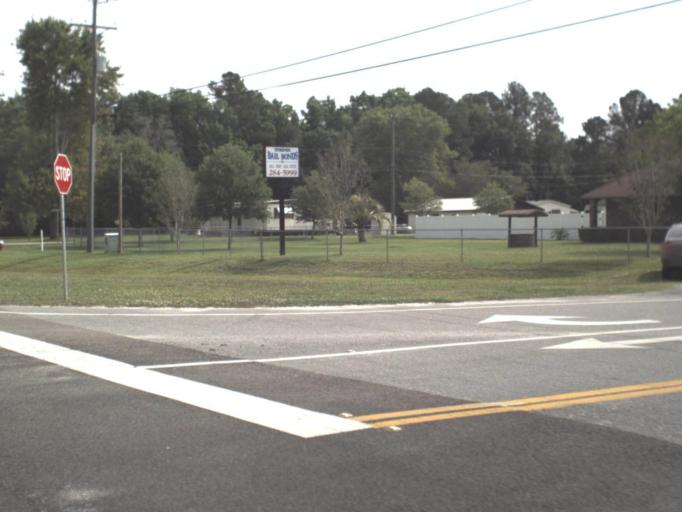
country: US
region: Florida
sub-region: Clay County
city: Green Cove Springs
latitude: 30.0334
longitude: -81.7089
